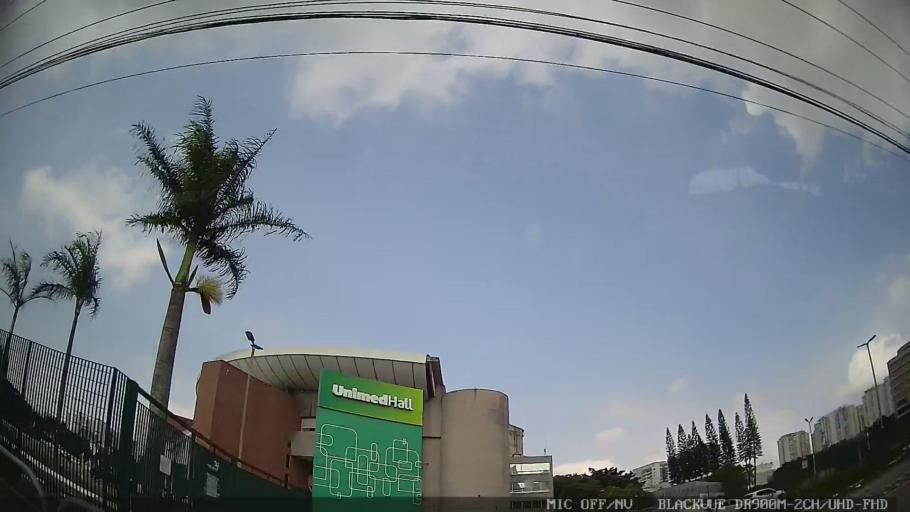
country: BR
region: Sao Paulo
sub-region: Taboao Da Serra
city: Taboao da Serra
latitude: -23.6484
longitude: -46.7248
